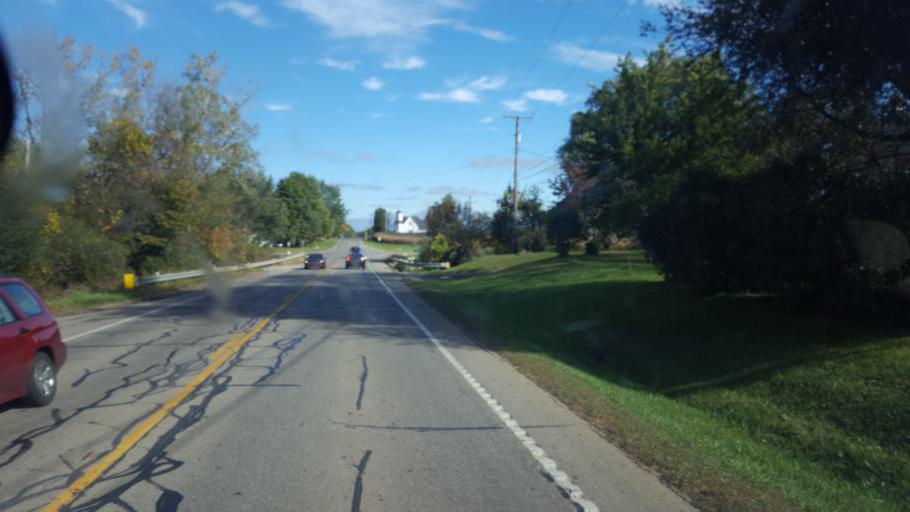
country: US
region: Ohio
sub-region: Richland County
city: Lincoln Heights
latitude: 40.8473
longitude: -82.5136
